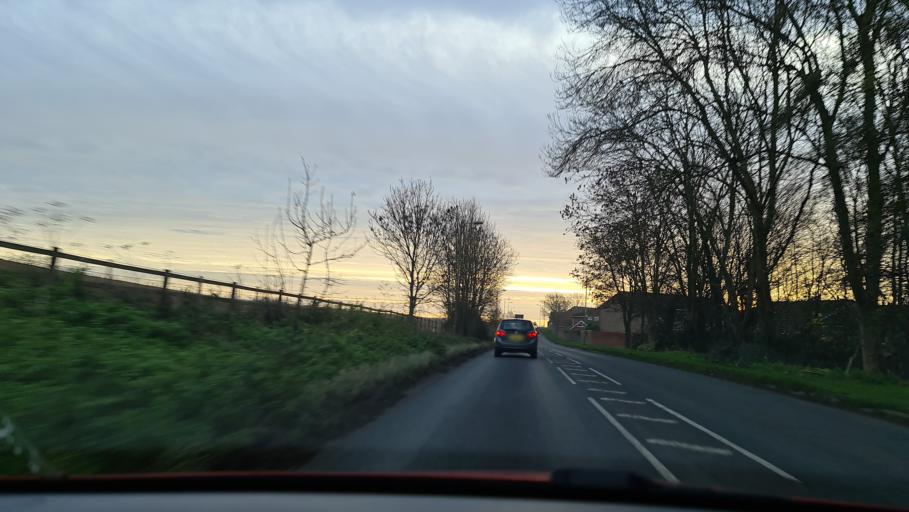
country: GB
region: England
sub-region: Oxfordshire
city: Thame
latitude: 51.7515
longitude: -0.9684
